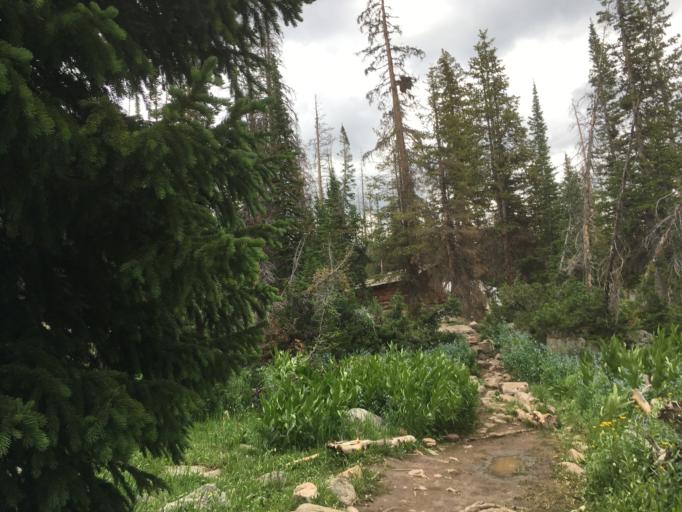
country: US
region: Utah
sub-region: Summit County
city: Kamas
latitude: 40.7192
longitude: -110.8827
